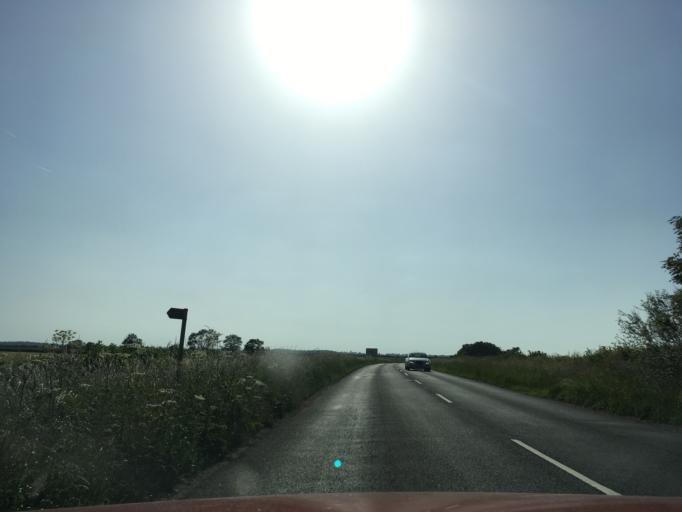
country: GB
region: England
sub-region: Oxfordshire
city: Somerton
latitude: 51.9159
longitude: -1.2709
